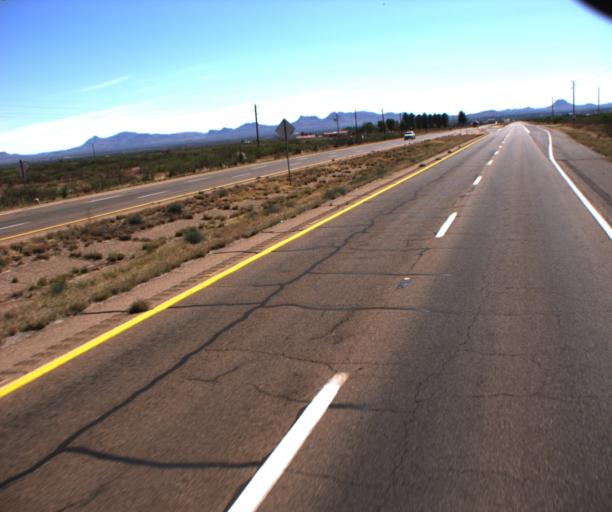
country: US
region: Arizona
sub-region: Cochise County
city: Pirtleville
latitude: 31.3573
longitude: -109.6329
